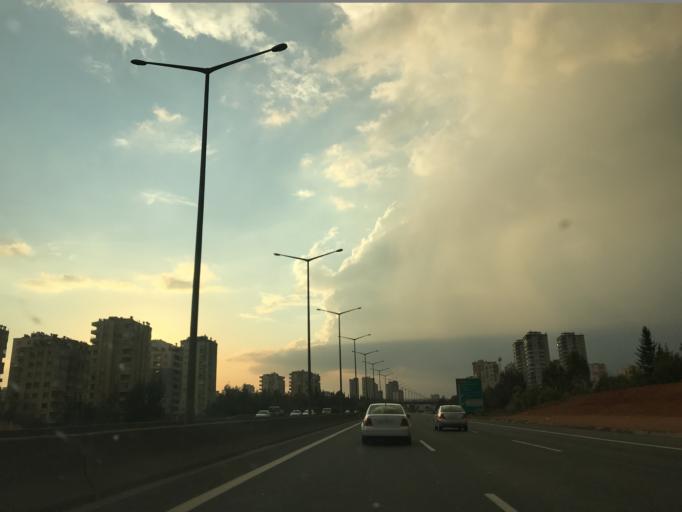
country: TR
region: Adana
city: Seyhan
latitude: 37.0303
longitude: 35.2710
